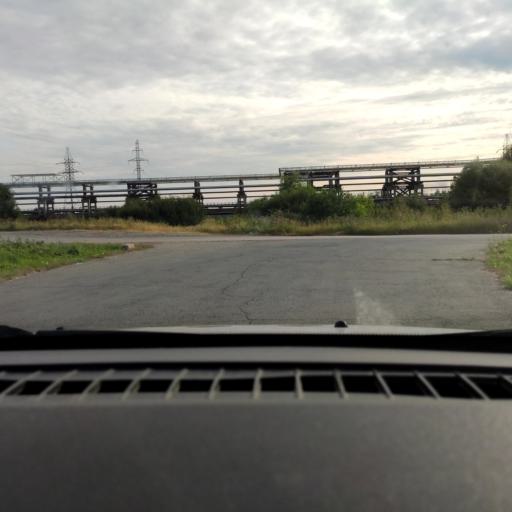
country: RU
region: Perm
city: Gamovo
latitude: 57.8868
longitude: 56.1631
